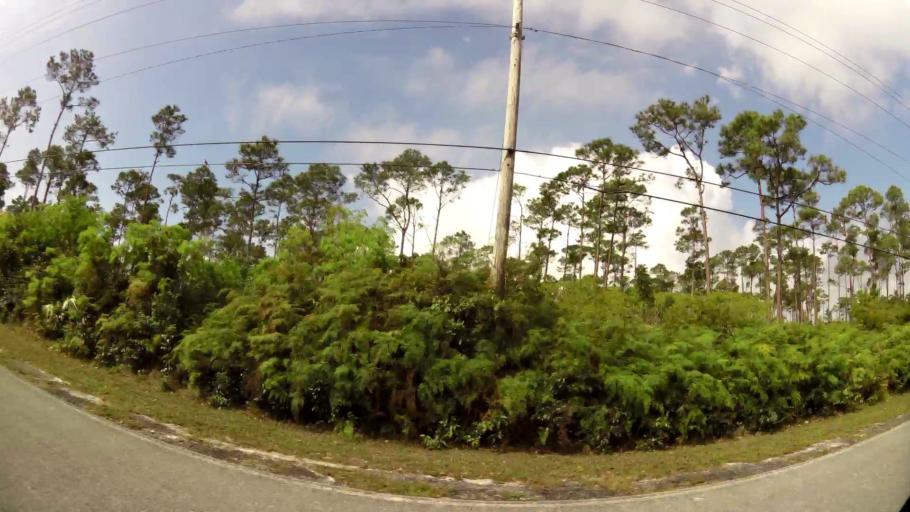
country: BS
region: Freeport
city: Lucaya
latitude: 26.5456
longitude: -78.5830
